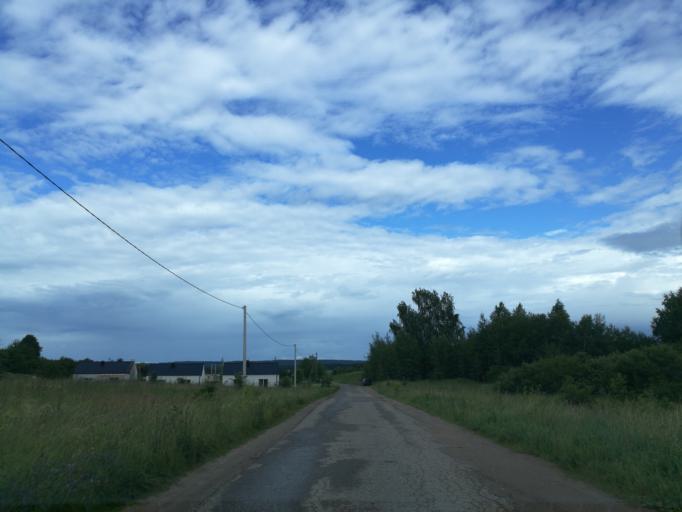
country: LT
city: Lentvaris
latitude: 54.6807
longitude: 25.0175
